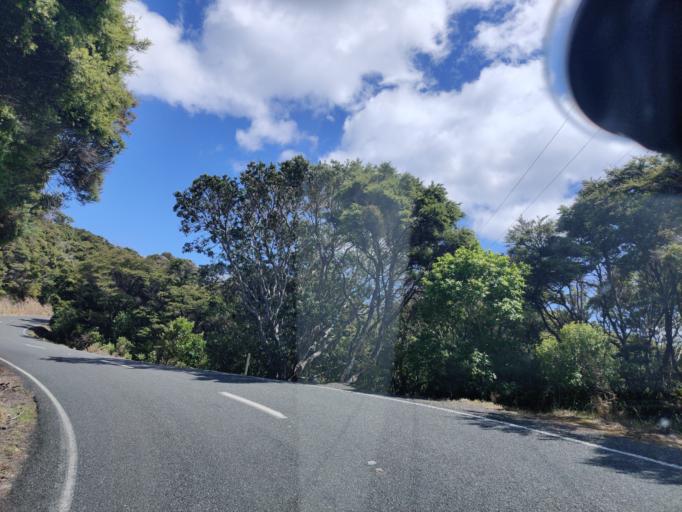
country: NZ
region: Northland
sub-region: Far North District
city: Paihia
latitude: -35.2603
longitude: 174.2458
